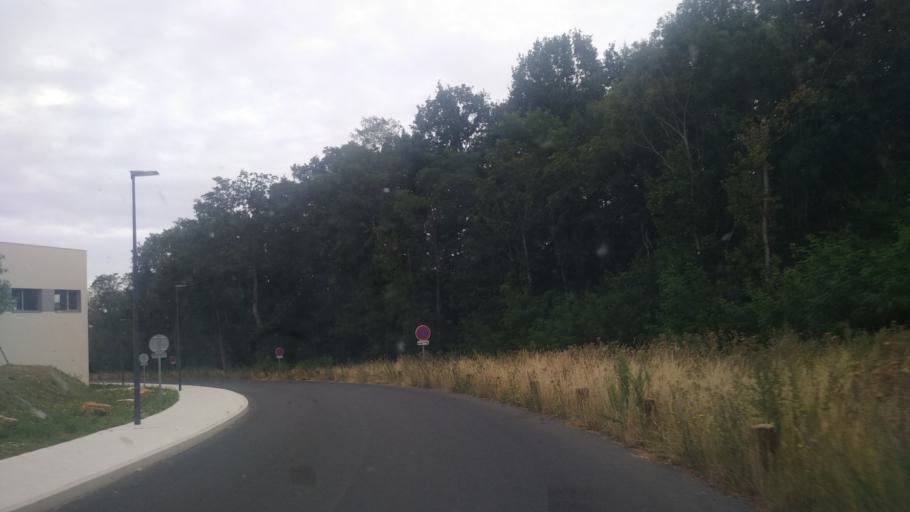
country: FR
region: Ile-de-France
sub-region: Departement de Seine-et-Marne
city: Voisenon
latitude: 48.5584
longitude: 2.6450
